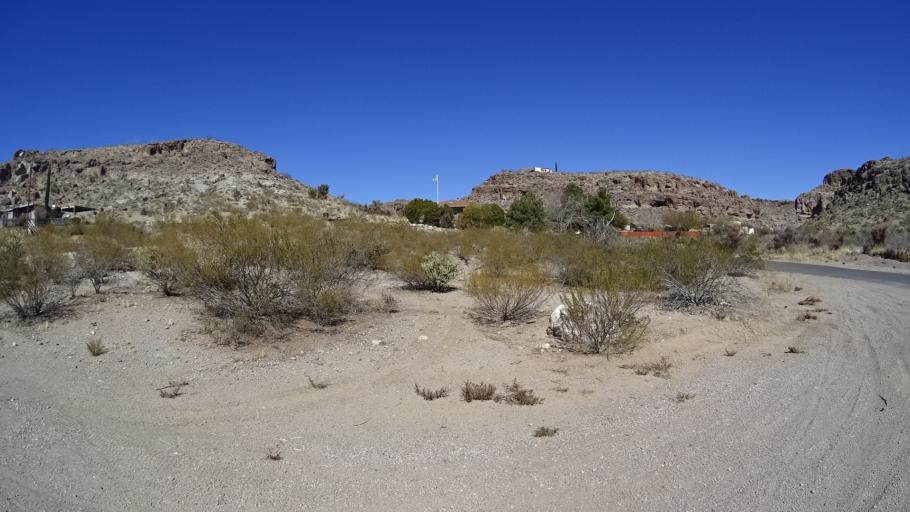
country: US
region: Arizona
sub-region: Mohave County
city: Kingman
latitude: 35.1991
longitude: -114.0599
